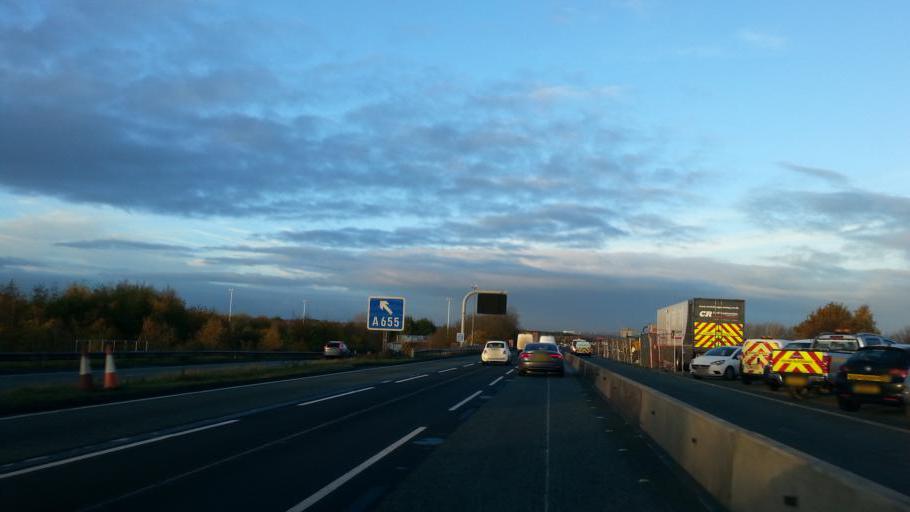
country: GB
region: England
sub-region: City and Borough of Wakefield
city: Normanton
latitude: 53.7084
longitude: -1.3922
